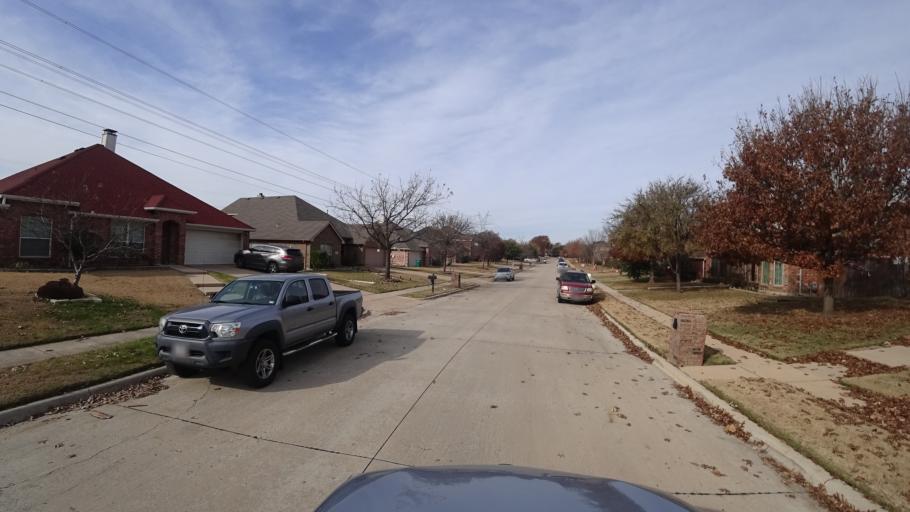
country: US
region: Texas
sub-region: Denton County
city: Highland Village
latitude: 33.0739
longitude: -97.0364
